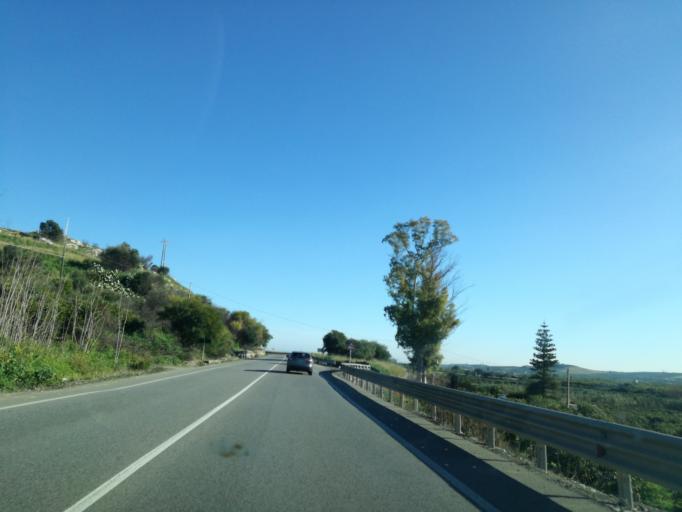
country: IT
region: Sicily
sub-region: Catania
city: Ramacca
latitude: 37.3642
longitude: 14.7166
